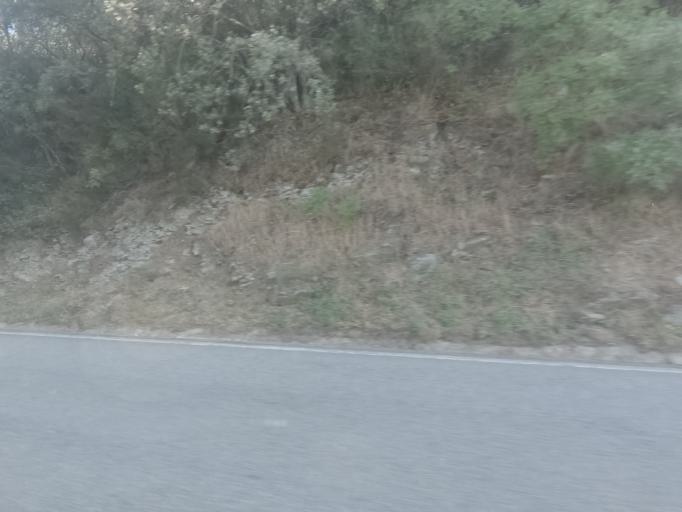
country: PT
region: Viseu
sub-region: Tabuaco
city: Tabuaco
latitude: 41.1572
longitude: -7.6047
